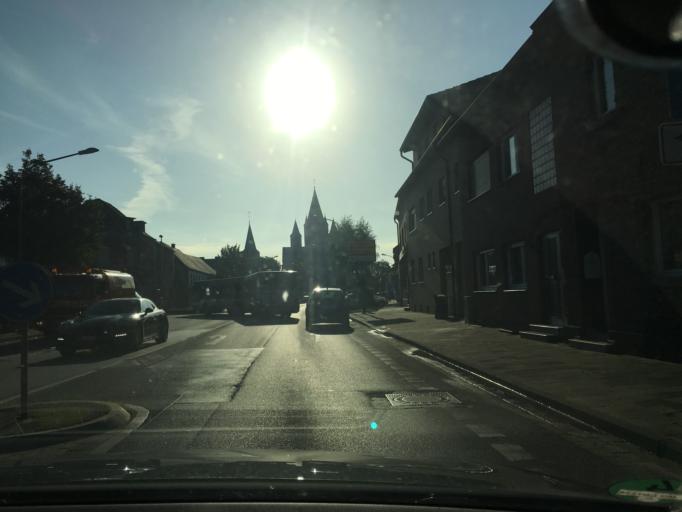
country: DE
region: North Rhine-Westphalia
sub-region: Regierungsbezirk Koln
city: Dueren
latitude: 50.8382
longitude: 6.4907
